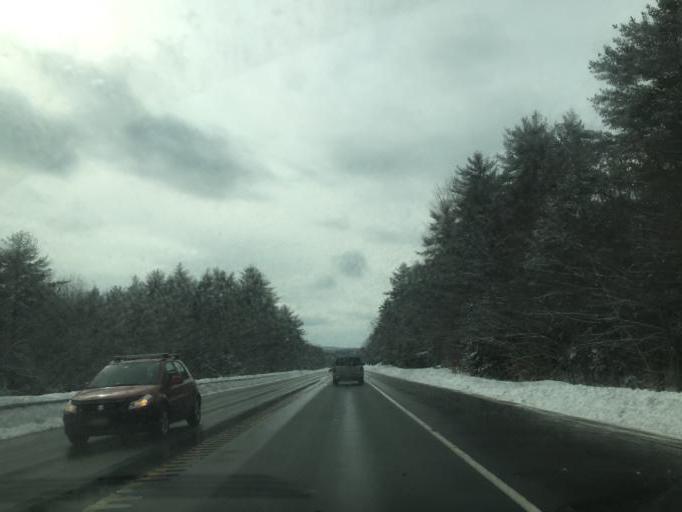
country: US
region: New Hampshire
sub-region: Carroll County
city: Sanbornville
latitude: 43.5129
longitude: -71.0287
